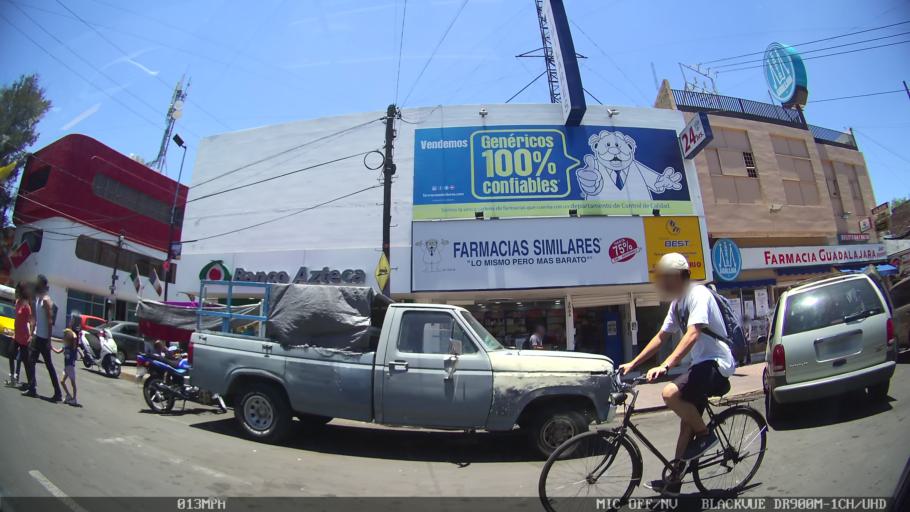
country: MX
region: Jalisco
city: Tlaquepaque
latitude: 20.6724
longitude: -103.2918
